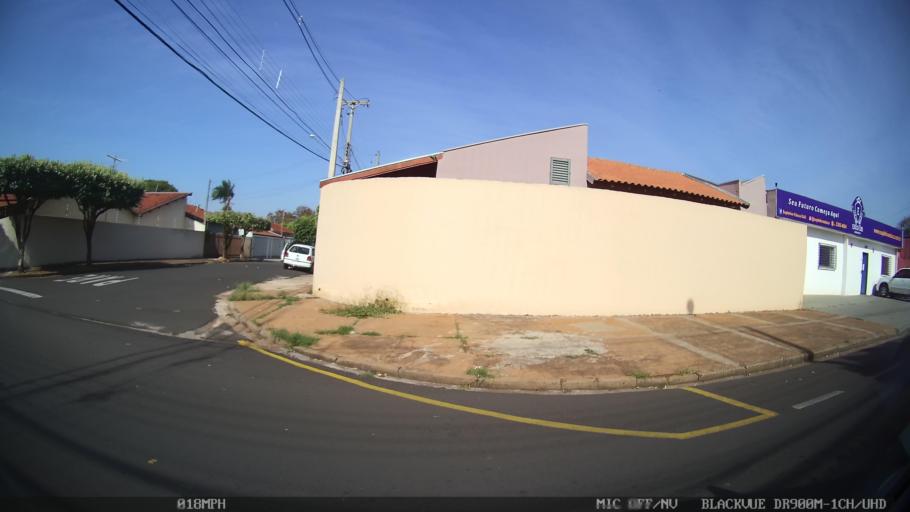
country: BR
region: Sao Paulo
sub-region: Sao Jose Do Rio Preto
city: Sao Jose do Rio Preto
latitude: -20.7957
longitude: -49.4093
